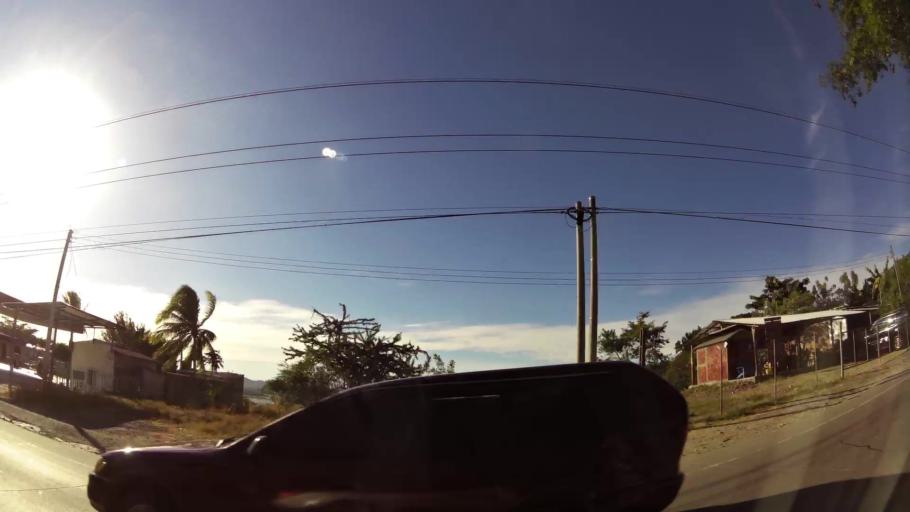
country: SV
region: Santa Ana
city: Metapan
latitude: 14.3077
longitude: -89.4532
